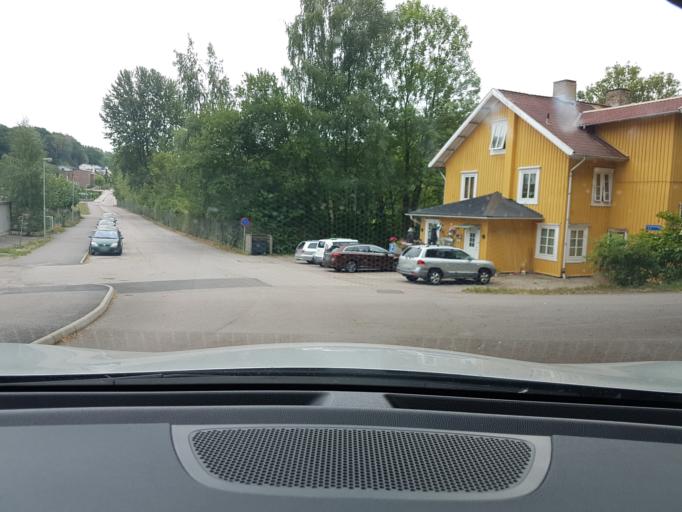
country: SE
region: Vaestra Goetaland
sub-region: Ale Kommun
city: Surte
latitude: 57.8312
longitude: 12.0188
